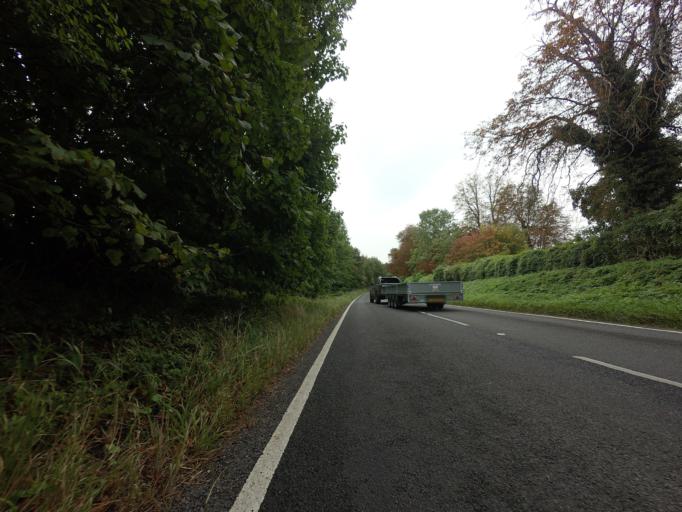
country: GB
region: England
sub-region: Hertfordshire
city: Reed
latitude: 52.0137
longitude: 0.0286
